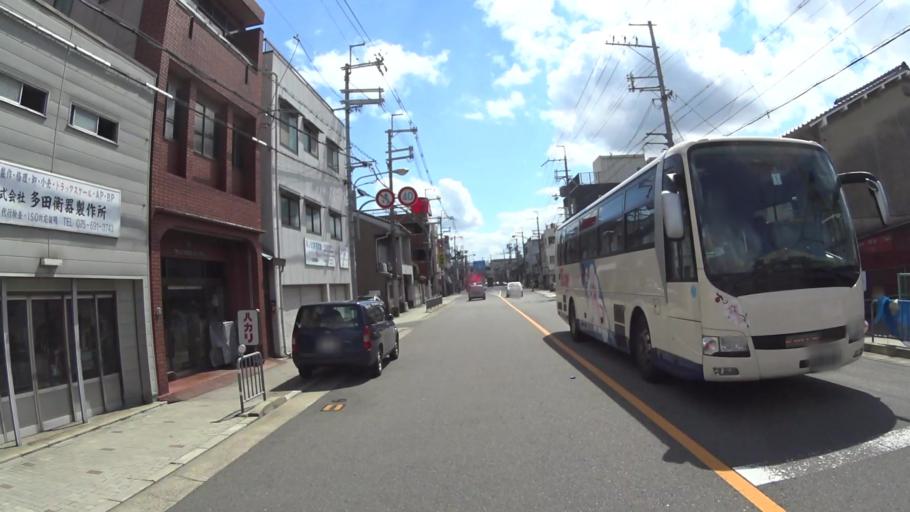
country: JP
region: Kyoto
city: Kyoto
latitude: 34.9750
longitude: 135.7618
